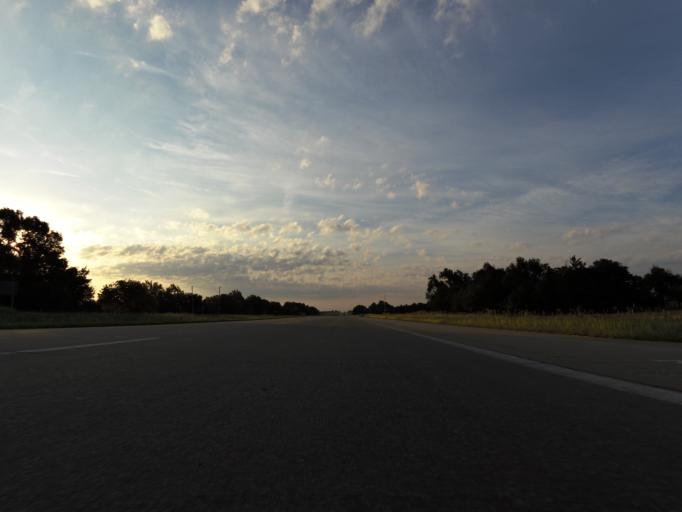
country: US
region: Kansas
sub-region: Reno County
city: Haven
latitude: 37.9297
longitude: -97.8500
